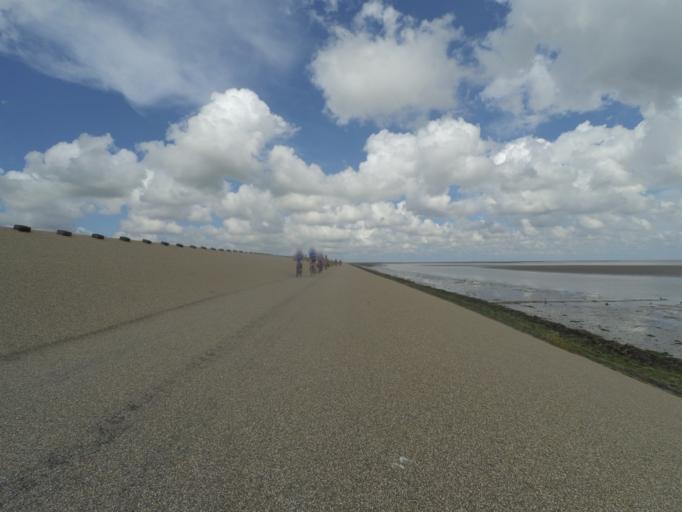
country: NL
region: North Holland
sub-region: Gemeente Texel
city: Den Burg
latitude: 53.1015
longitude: 4.8982
